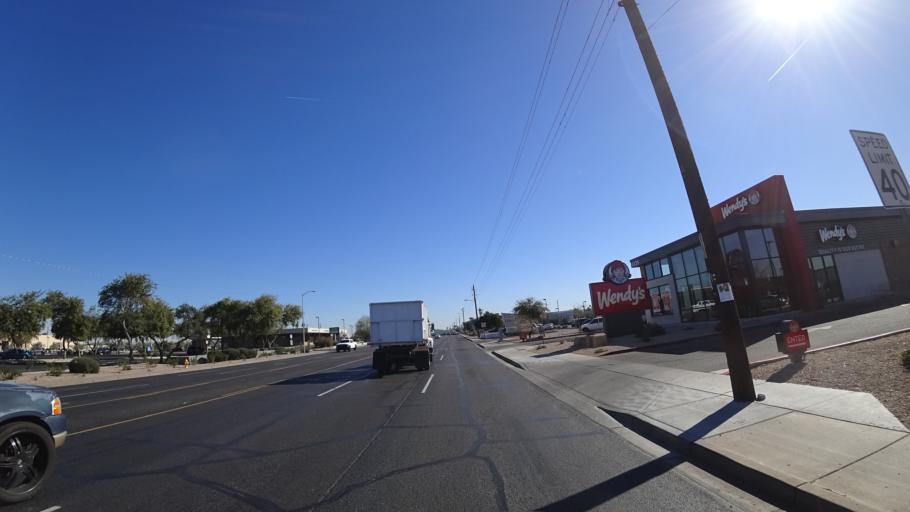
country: US
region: Arizona
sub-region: Maricopa County
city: Glendale
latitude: 33.4949
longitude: -112.1720
